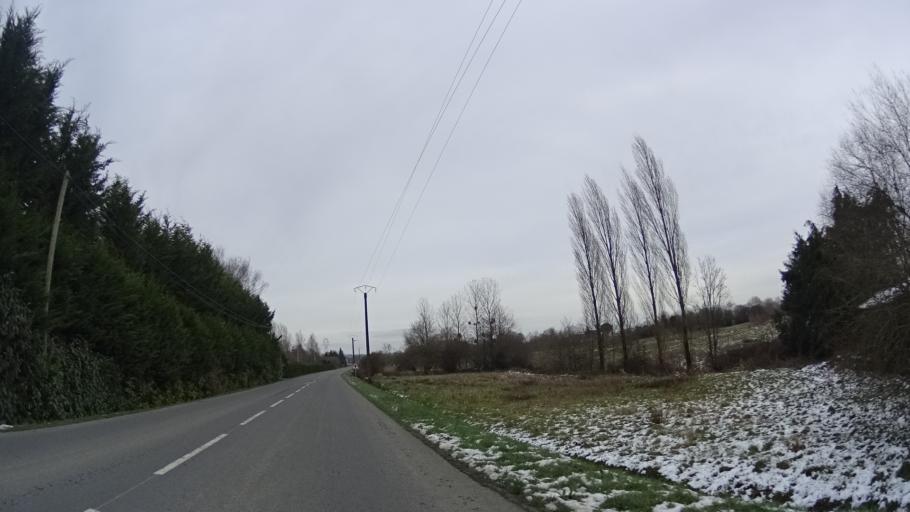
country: FR
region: Brittany
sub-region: Departement d'Ille-et-Vilaine
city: Montauban-de-Bretagne
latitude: 48.2334
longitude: -2.0169
